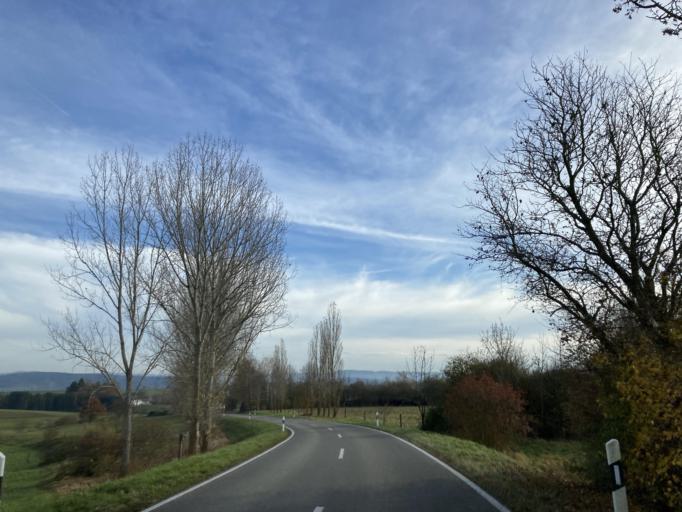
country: DE
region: Baden-Wuerttemberg
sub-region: Tuebingen Region
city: Hirrlingen
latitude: 48.4110
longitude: 8.8404
